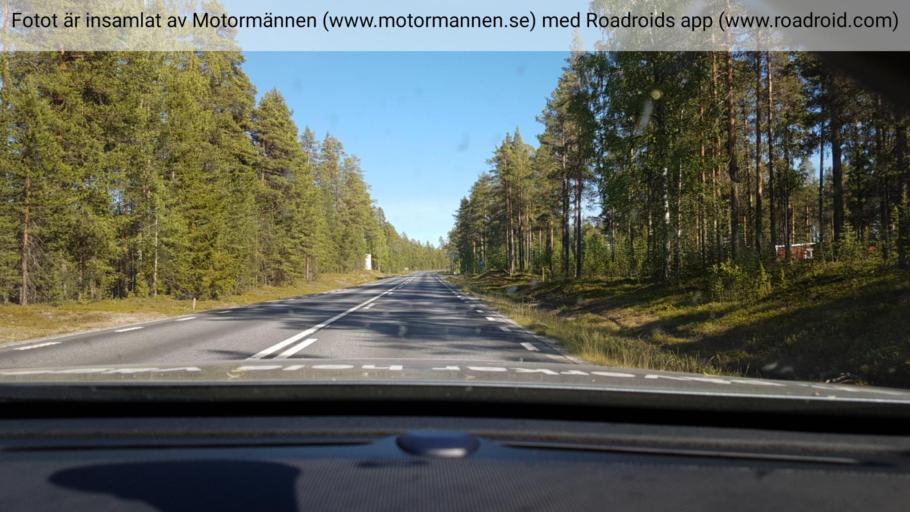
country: SE
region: Vaesterbotten
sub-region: Lycksele Kommun
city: Lycksele
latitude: 64.5225
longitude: 18.8207
